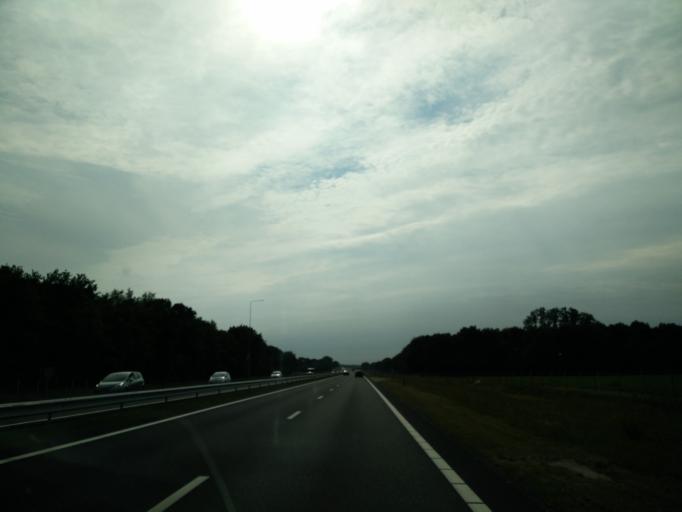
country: NL
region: Drenthe
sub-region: Gemeente Assen
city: Assen
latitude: 52.9699
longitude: 6.6030
